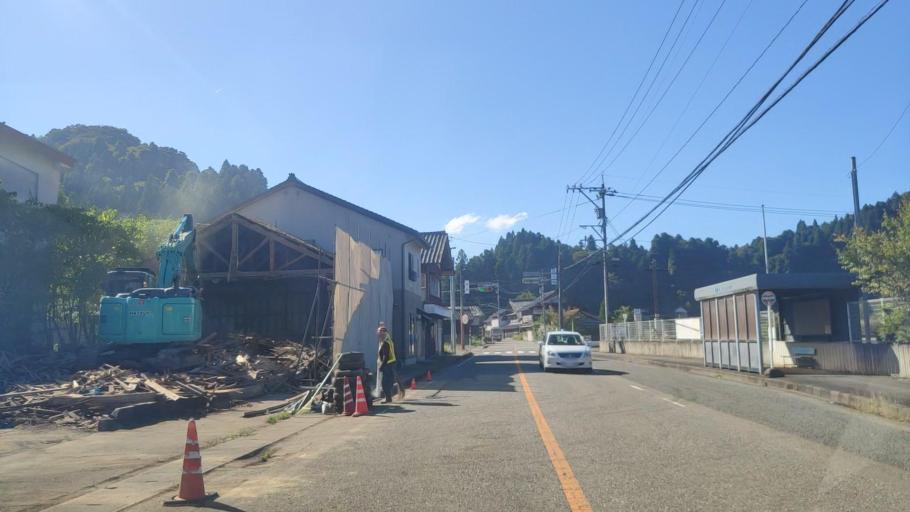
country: JP
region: Ishikawa
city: Nanao
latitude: 37.2816
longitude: 137.0412
